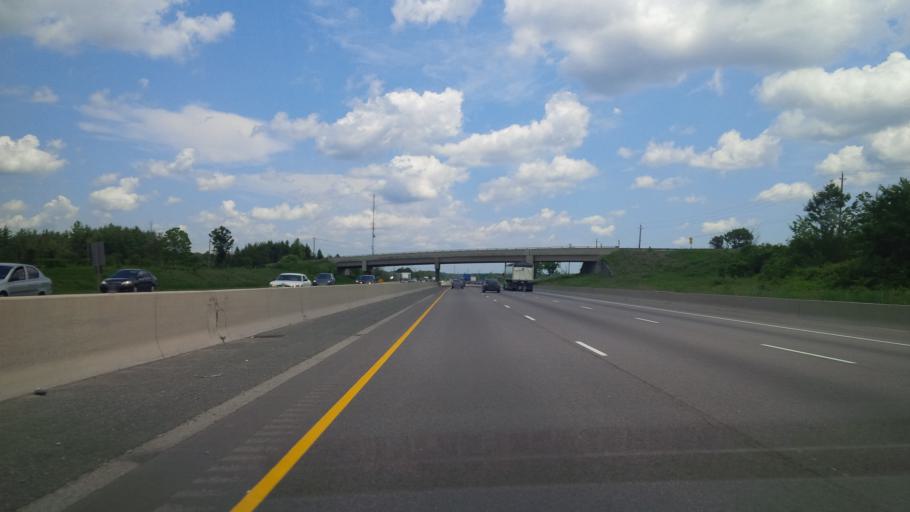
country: CA
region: Ontario
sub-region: Wellington County
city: Guelph
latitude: 43.4602
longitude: -80.1033
